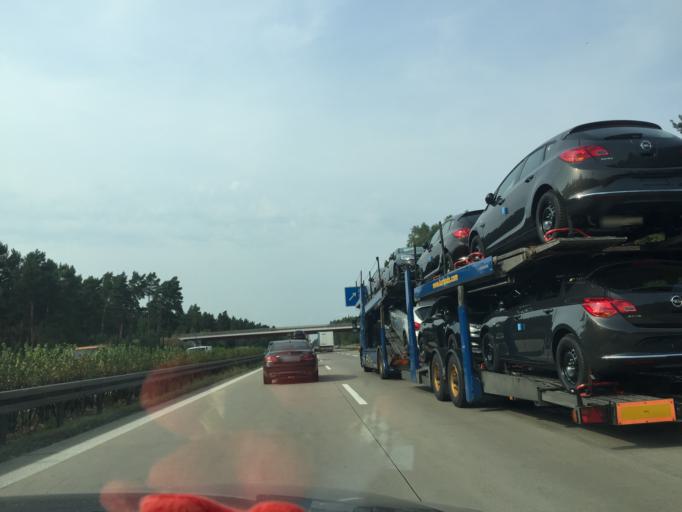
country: DE
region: Brandenburg
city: Halbe
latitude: 52.0609
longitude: 13.6534
